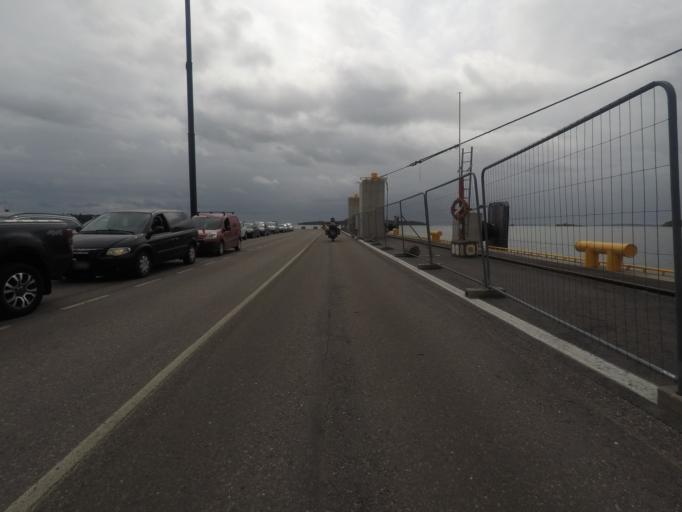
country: FI
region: Uusimaa
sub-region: Helsinki
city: Helsinki
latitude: 60.1490
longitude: 24.9118
